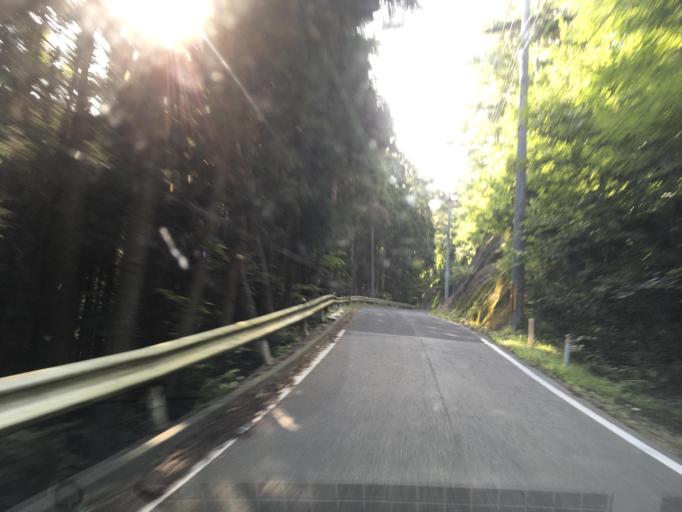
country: JP
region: Iwate
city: Ofunato
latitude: 38.9150
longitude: 141.6161
